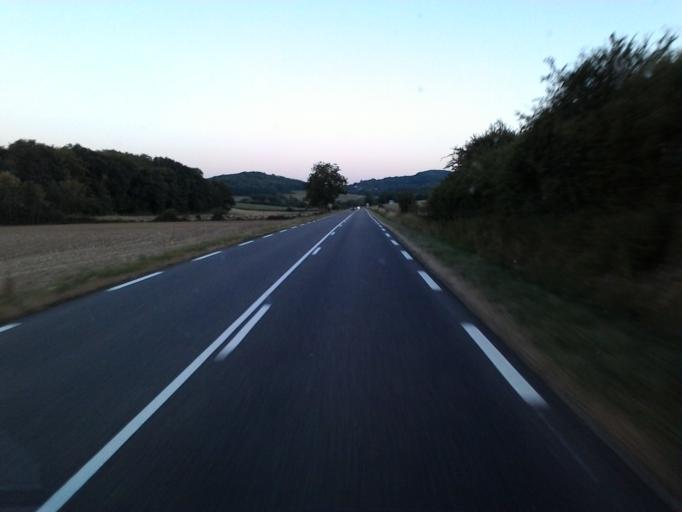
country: FR
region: Franche-Comte
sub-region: Departement du Jura
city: Poligny
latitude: 46.8232
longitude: 5.5948
